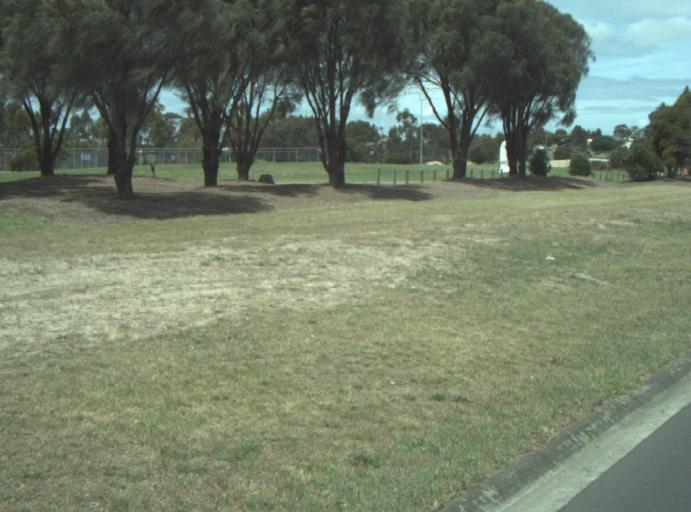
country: AU
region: Victoria
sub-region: Greater Geelong
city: Wandana Heights
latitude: -38.1989
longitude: 144.3208
